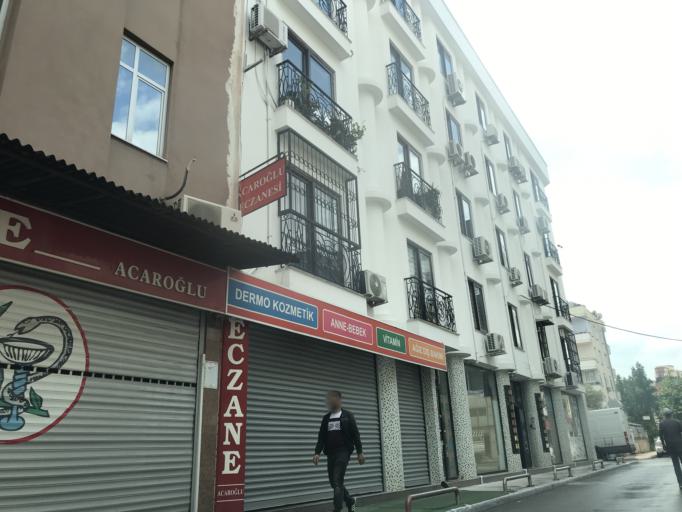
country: TR
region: Mersin
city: Mercin
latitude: 36.8019
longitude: 34.6296
